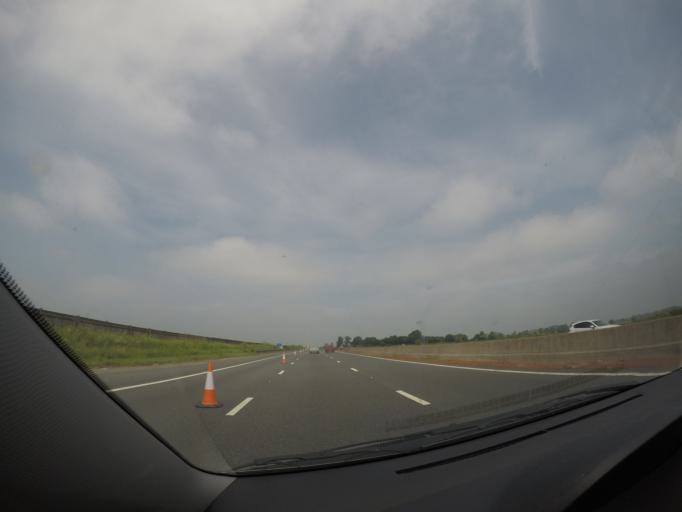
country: GB
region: England
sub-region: North Yorkshire
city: Ripon
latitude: 54.2034
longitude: -1.4725
